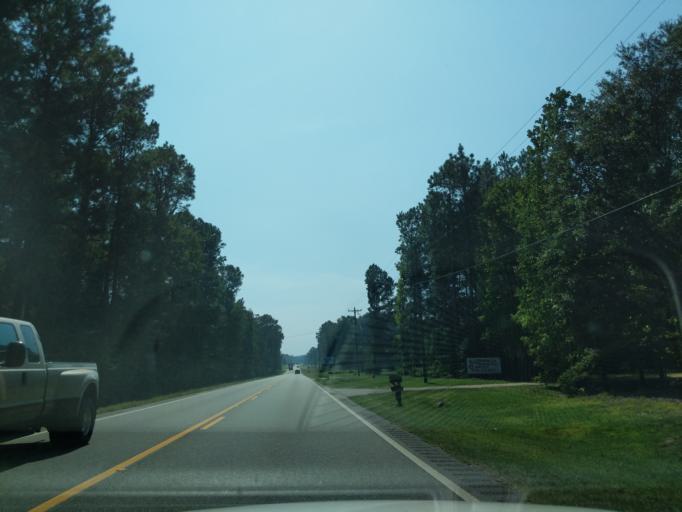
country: US
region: Alabama
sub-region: Covington County
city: Andalusia
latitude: 31.2670
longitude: -86.5124
